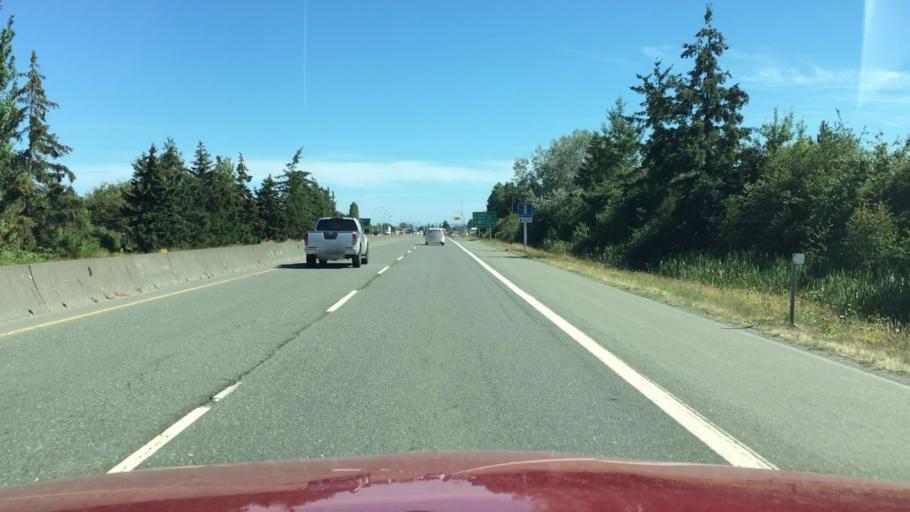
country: CA
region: British Columbia
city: North Saanich
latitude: 48.6531
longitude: -123.4102
